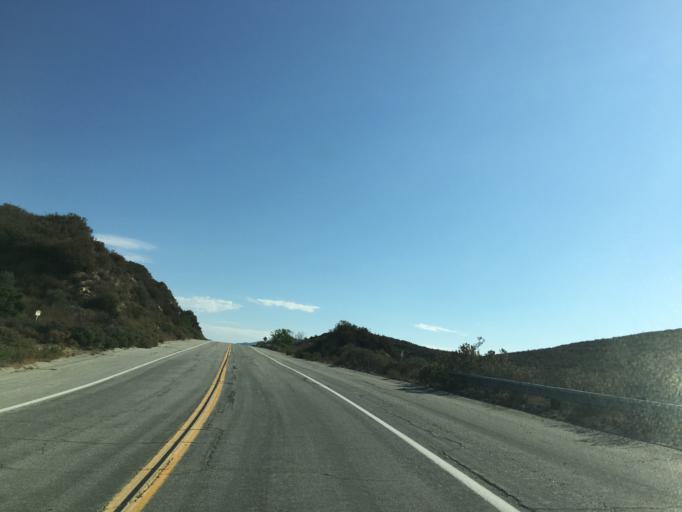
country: US
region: California
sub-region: Los Angeles County
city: Castaic
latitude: 34.5733
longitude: -118.6733
